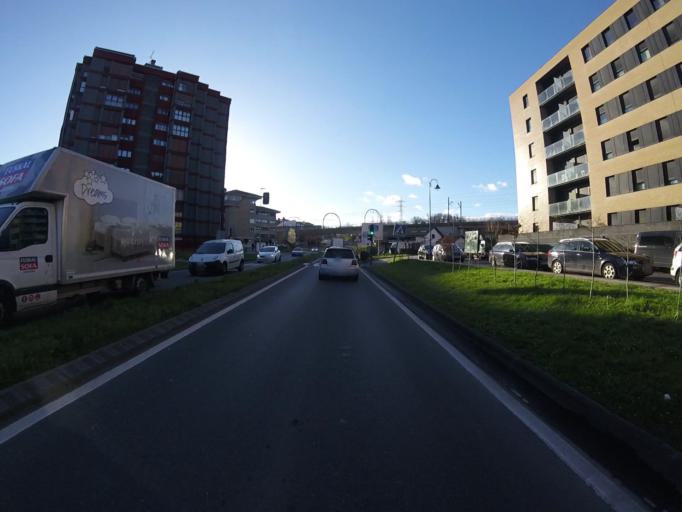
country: ES
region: Basque Country
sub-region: Provincia de Guipuzcoa
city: Lezo
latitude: 43.3091
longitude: -1.8826
